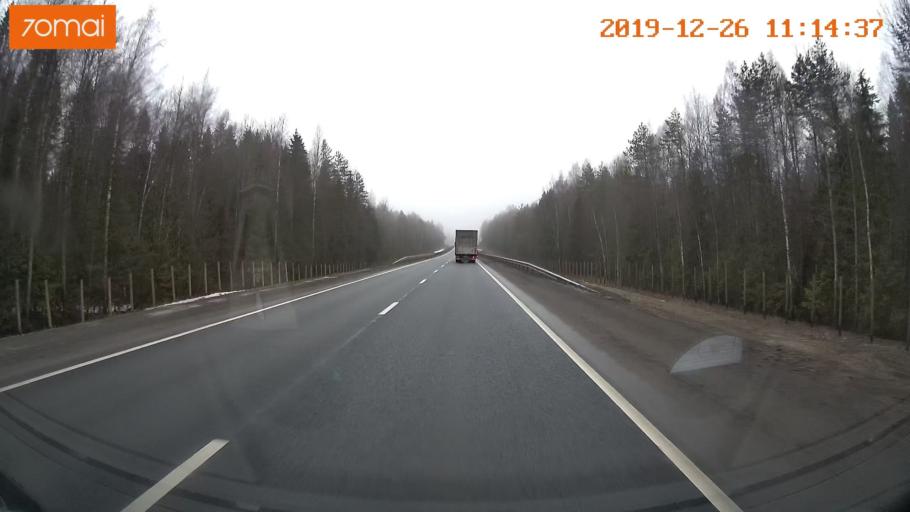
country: RU
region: Vologda
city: Chebsara
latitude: 59.1210
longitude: 39.1222
